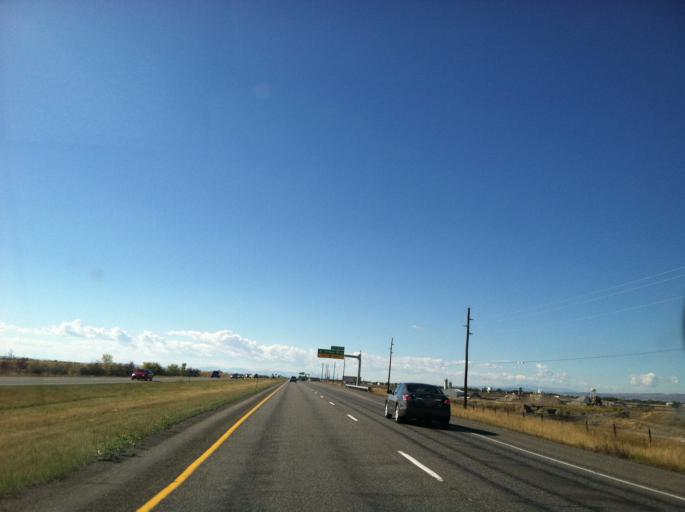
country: US
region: Montana
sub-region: Gallatin County
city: Belgrade
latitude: 45.7548
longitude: -111.1469
